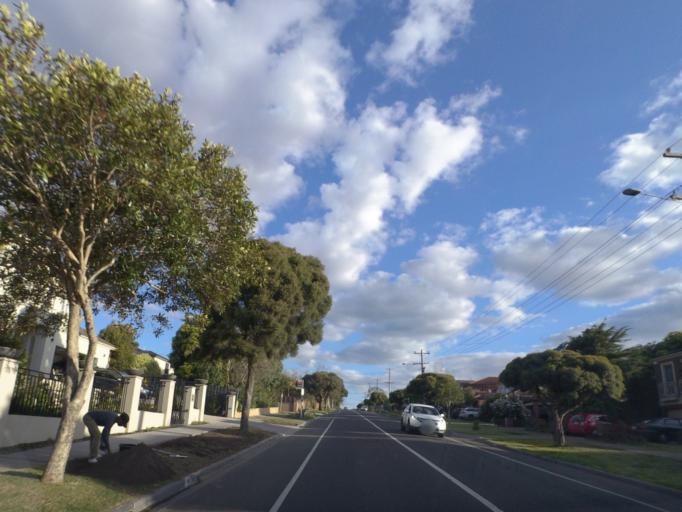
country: AU
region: Victoria
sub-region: Boroondara
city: Balwyn North
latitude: -37.7923
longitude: 145.0994
